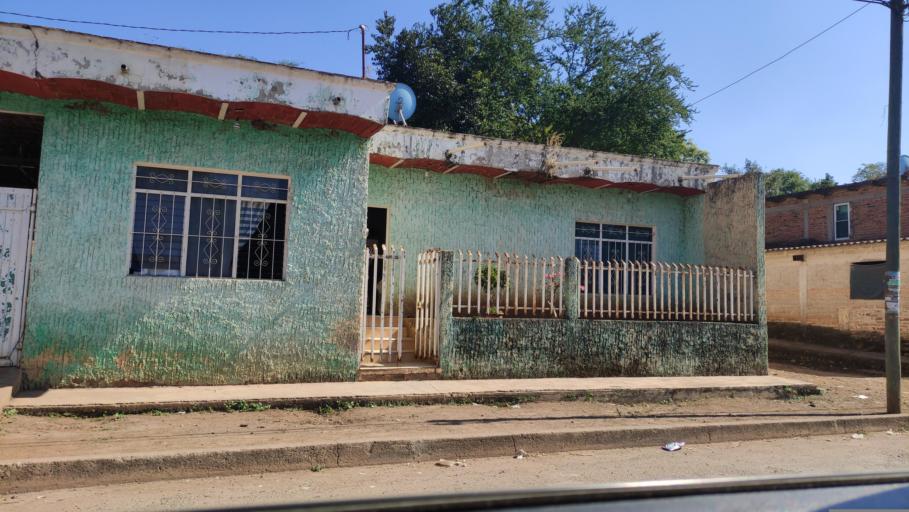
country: MX
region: Nayarit
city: Santa Maria del Oro
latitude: 21.3762
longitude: -104.6219
